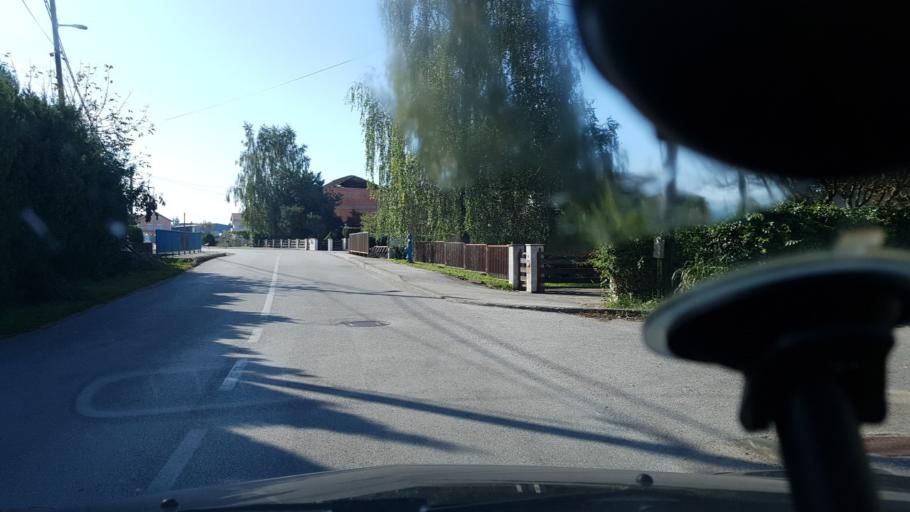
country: HR
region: Grad Zagreb
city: Jezdovec
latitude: 45.7581
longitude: 15.8339
